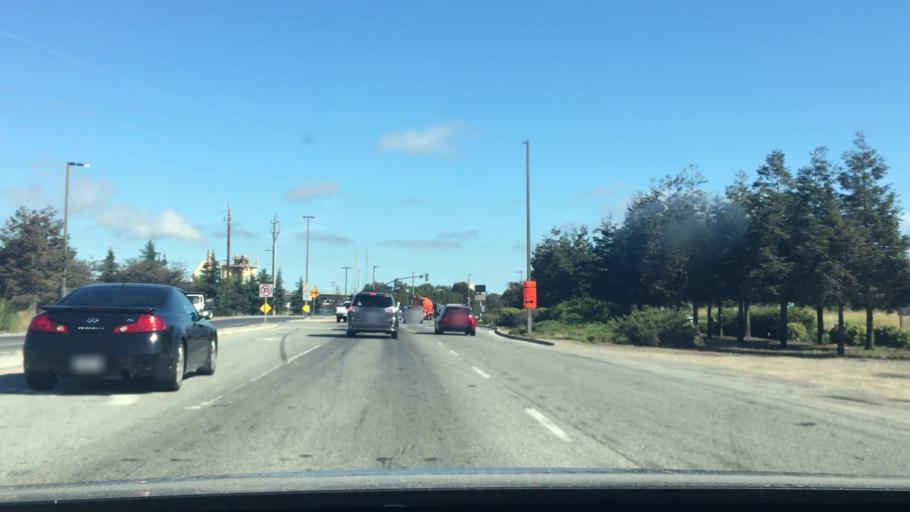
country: US
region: California
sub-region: San Mateo County
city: North Fair Oaks
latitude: 37.4922
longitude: -122.2121
